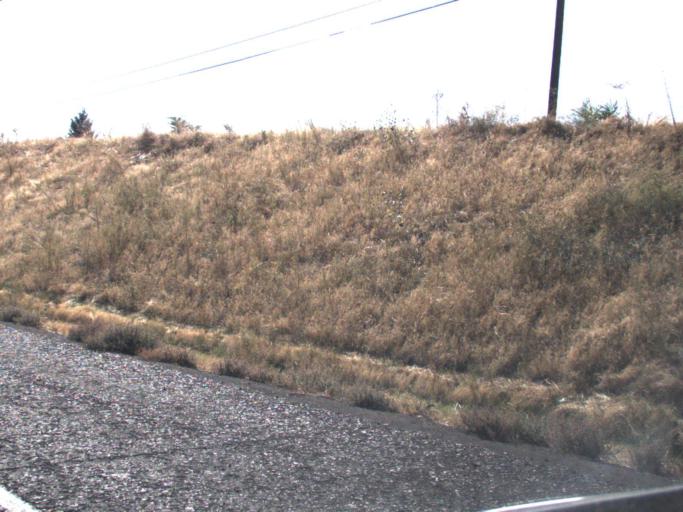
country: US
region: Washington
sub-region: Walla Walla County
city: College Place
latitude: 46.0252
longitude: -118.3890
